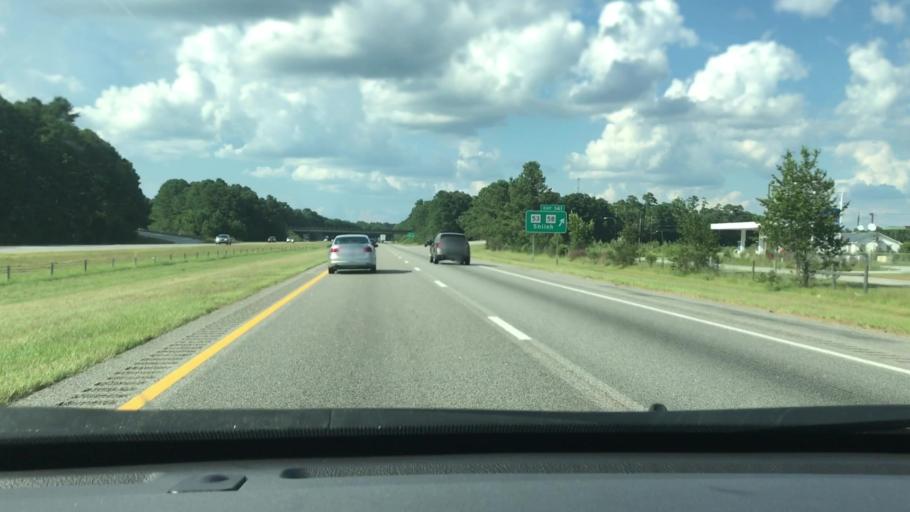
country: US
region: South Carolina
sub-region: Florence County
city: Timmonsville
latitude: 33.9651
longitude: -80.0434
